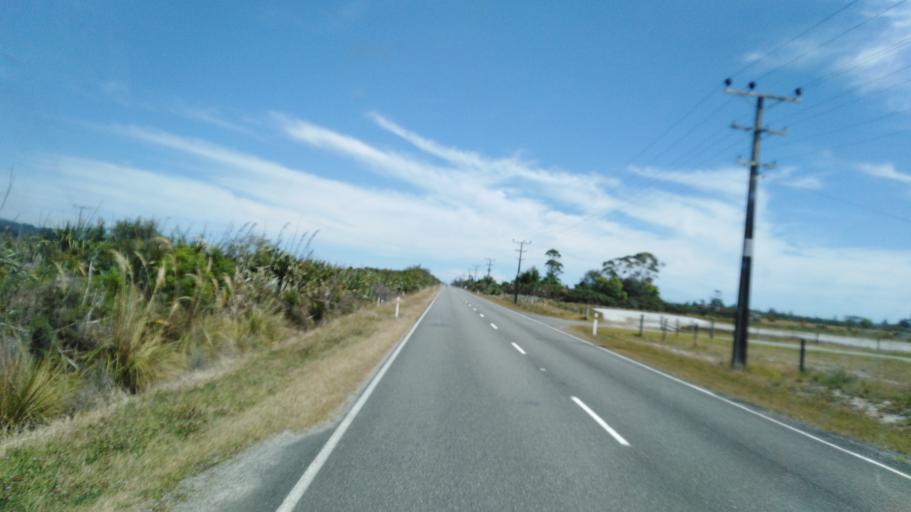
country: NZ
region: West Coast
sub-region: Buller District
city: Westport
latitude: -41.7470
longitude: 171.6815
